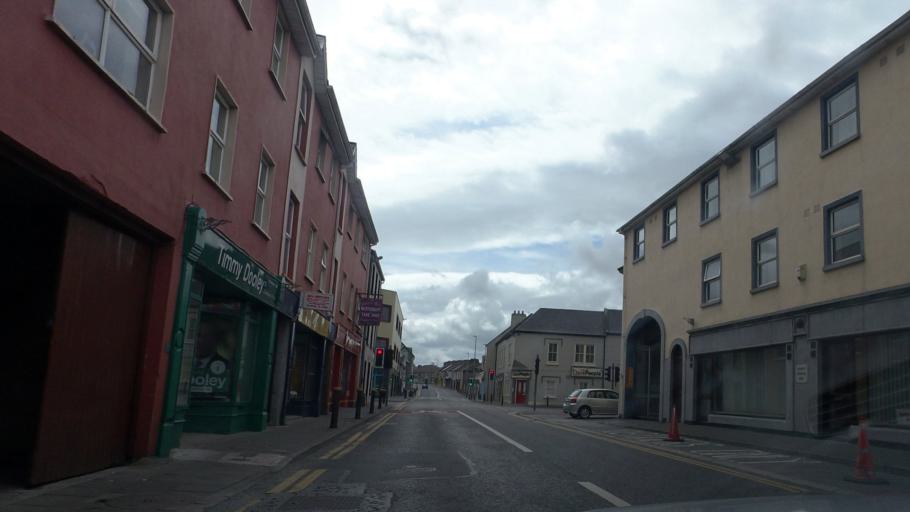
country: IE
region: Munster
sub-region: An Clar
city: Ennis
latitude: 52.8445
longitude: -8.9885
